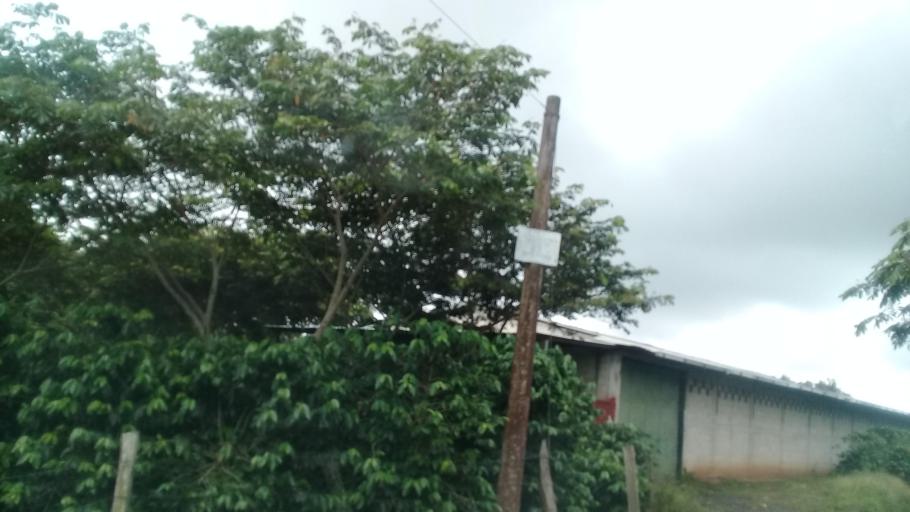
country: MX
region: Veracruz
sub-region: Xalapa
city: Colonia Santa Barbara
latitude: 19.4946
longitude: -96.8703
